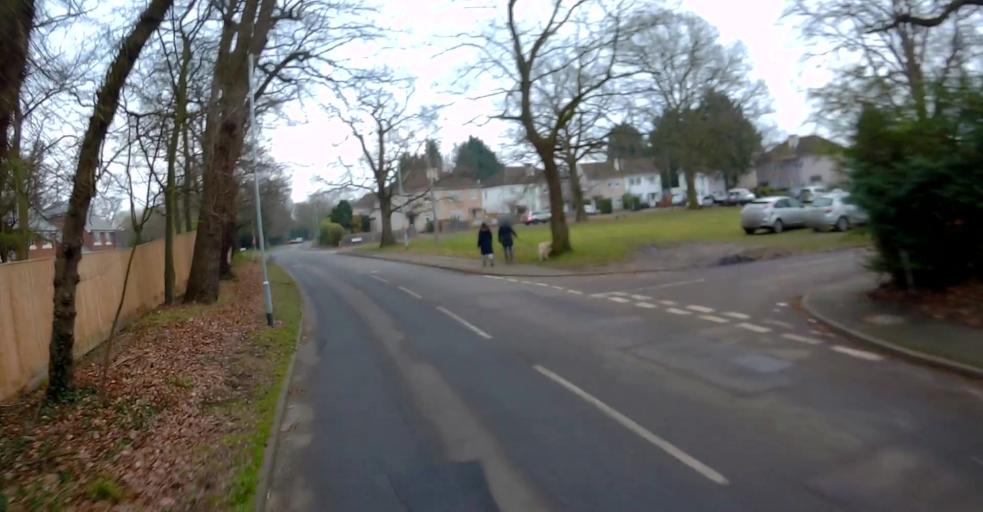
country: GB
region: England
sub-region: Wokingham
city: Wokingham
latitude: 51.4060
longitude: -0.8156
